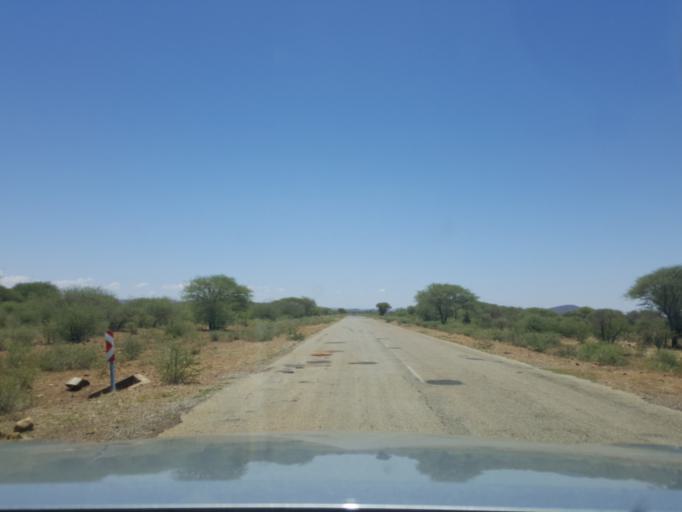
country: BW
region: South East
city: Ramotswa
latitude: -25.0169
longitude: 25.9090
